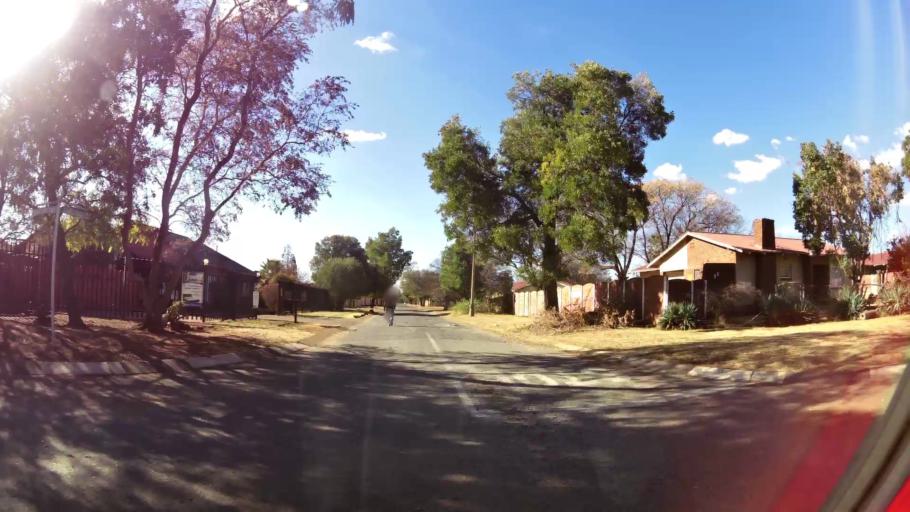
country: ZA
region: Gauteng
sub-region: West Rand District Municipality
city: Carletonville
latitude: -26.3642
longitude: 27.3773
